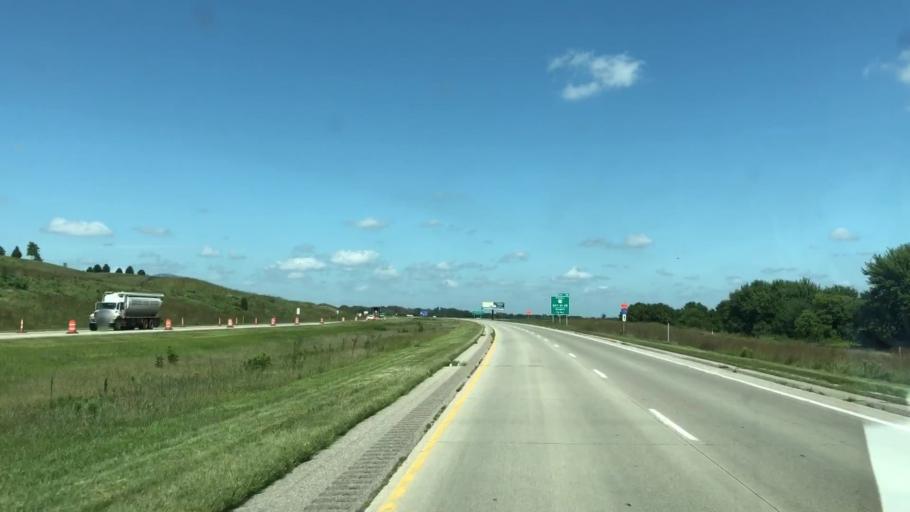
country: US
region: Iowa
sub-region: Plymouth County
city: Le Mars
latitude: 42.7506
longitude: -96.2108
